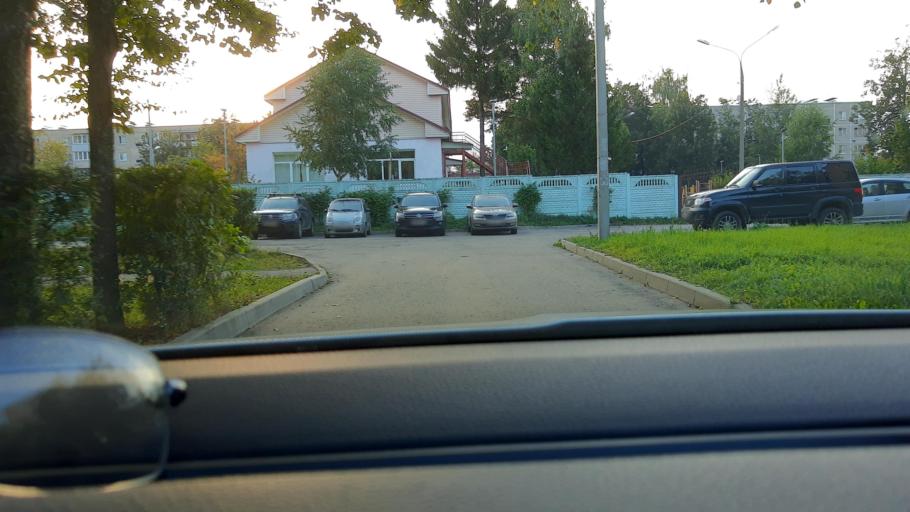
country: RU
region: Moskovskaya
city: Troitsk
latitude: 55.3166
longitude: 37.1785
